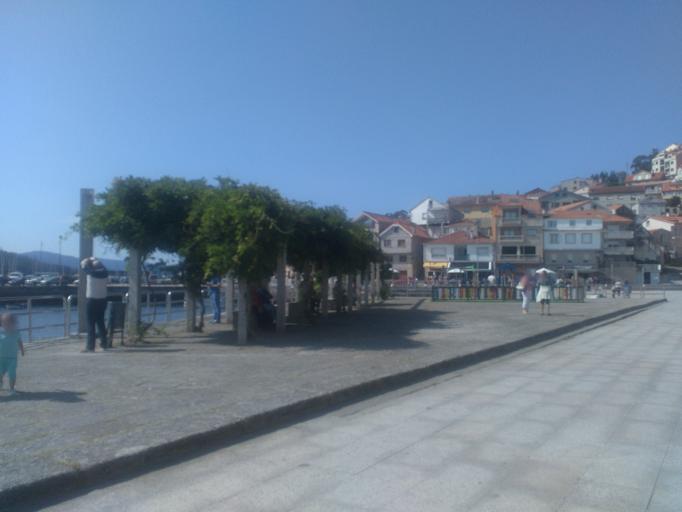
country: ES
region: Galicia
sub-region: Provincia de Pontevedra
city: Combarro
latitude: 42.4312
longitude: -8.7048
